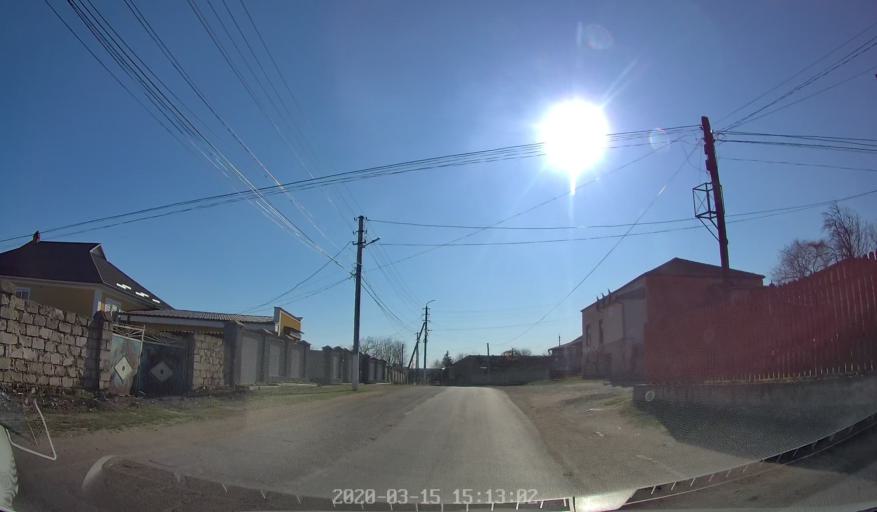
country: MD
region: Orhei
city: Orhei
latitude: 47.2518
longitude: 28.7725
